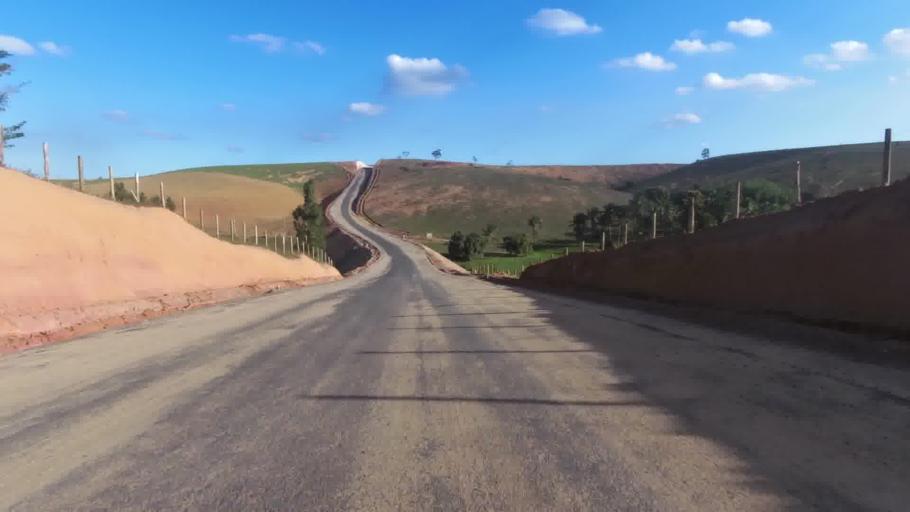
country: BR
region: Espirito Santo
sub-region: Marataizes
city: Marataizes
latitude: -21.1129
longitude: -41.0480
